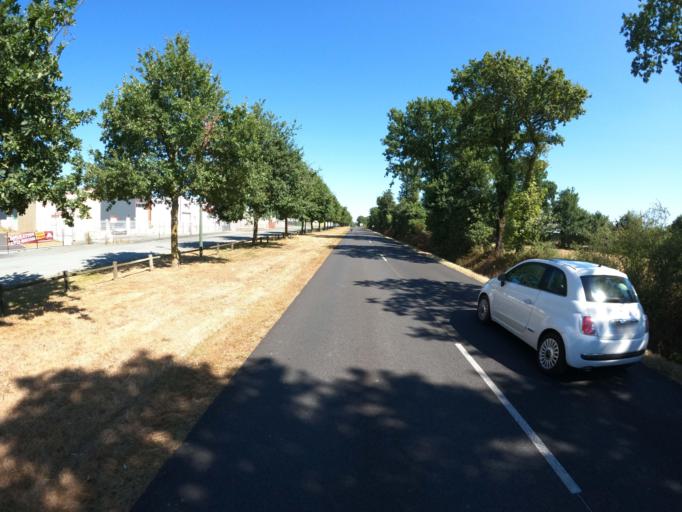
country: FR
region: Pays de la Loire
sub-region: Departement de la Vendee
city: La Guyonniere
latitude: 46.9611
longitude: -1.2576
